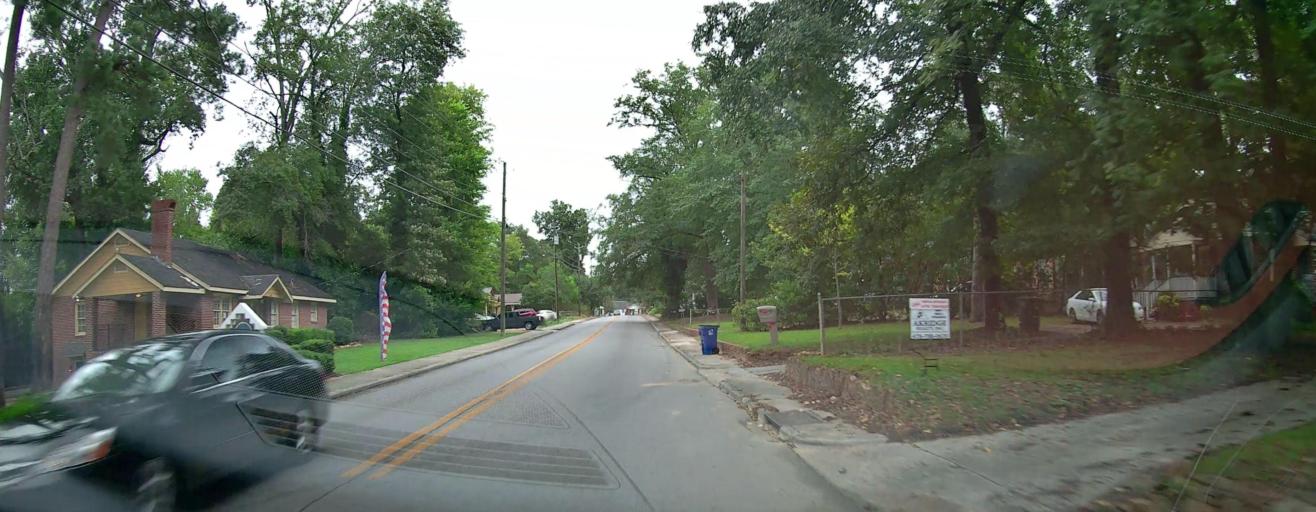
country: US
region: Georgia
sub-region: Bibb County
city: Macon
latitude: 32.8361
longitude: -83.6869
